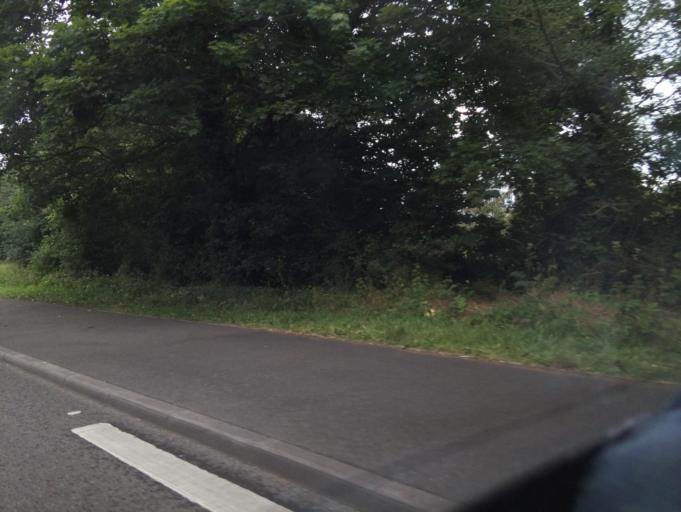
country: GB
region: England
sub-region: Dudley
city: Kingswinford
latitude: 52.4998
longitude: -2.1847
